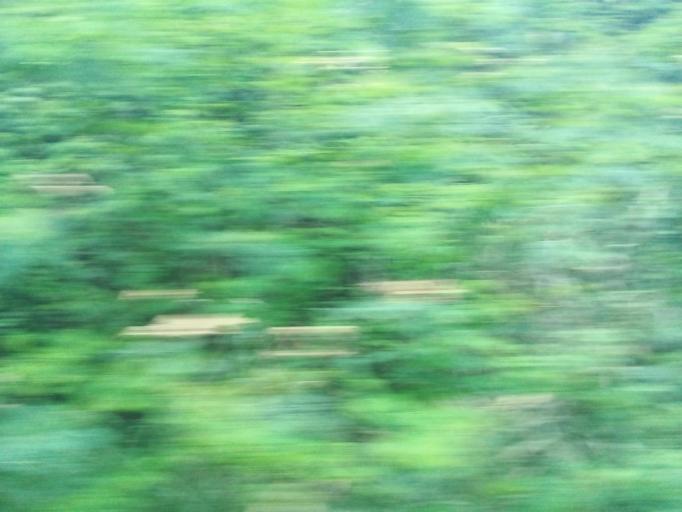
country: BR
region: Minas Gerais
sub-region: Joao Monlevade
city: Joao Monlevade
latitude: -19.8250
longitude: -43.1034
